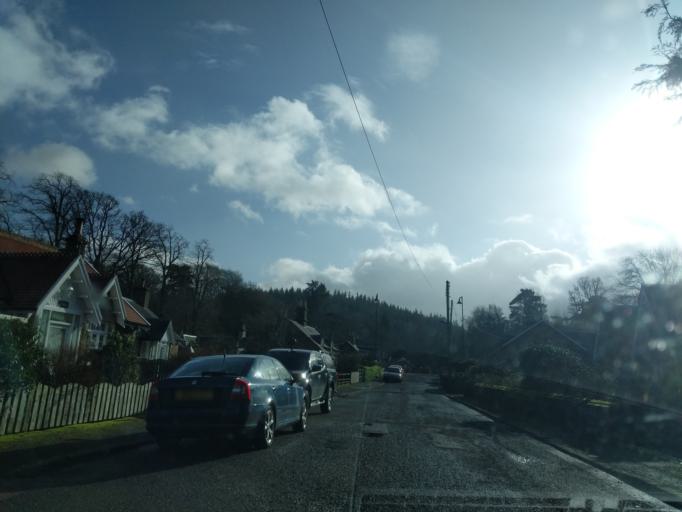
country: GB
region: Scotland
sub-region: South Lanarkshire
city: Biggar
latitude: 55.5632
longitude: -3.6193
